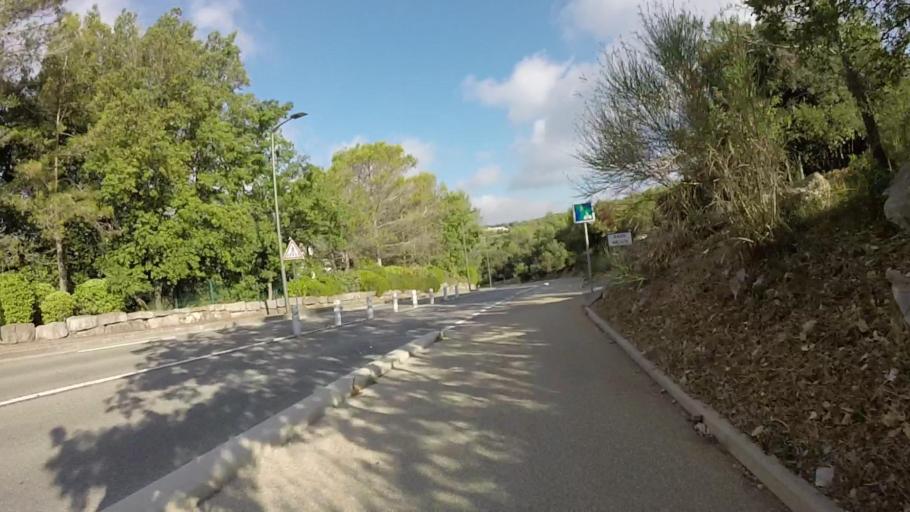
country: FR
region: Provence-Alpes-Cote d'Azur
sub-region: Departement des Alpes-Maritimes
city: Biot
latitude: 43.6242
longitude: 7.0585
